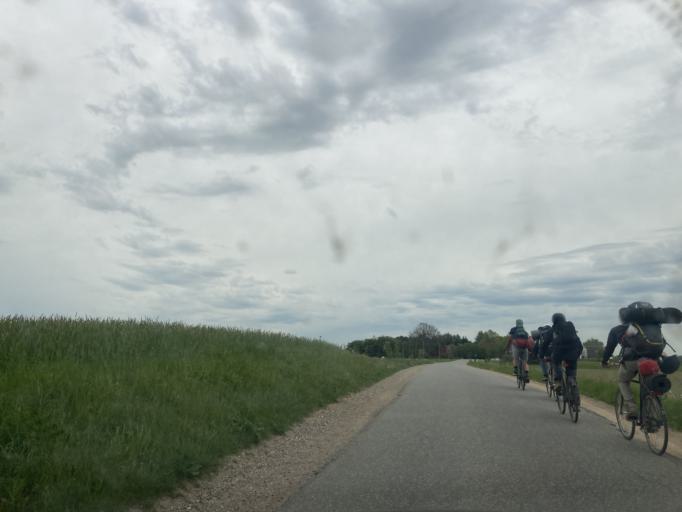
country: DK
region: Zealand
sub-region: Roskilde Kommune
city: Svogerslev
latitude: 55.6490
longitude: 11.9885
